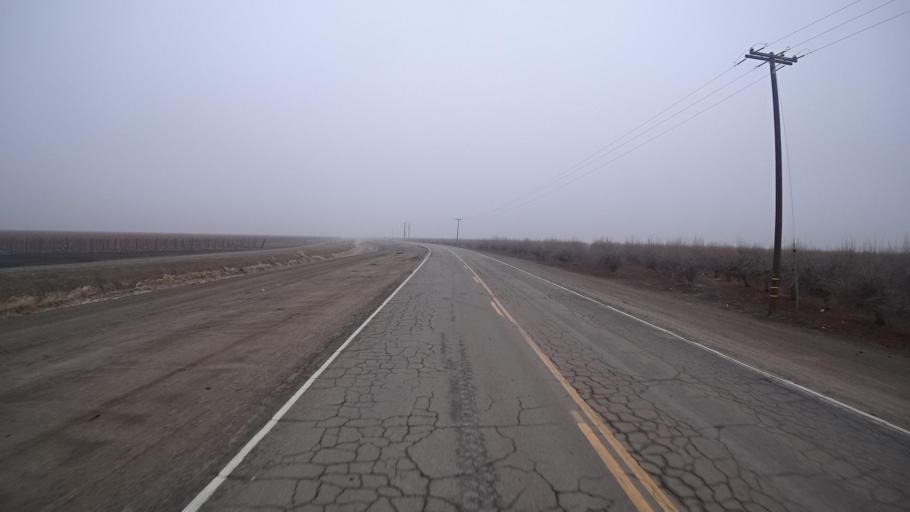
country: US
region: California
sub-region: Kern County
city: Lost Hills
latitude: 35.5131
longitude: -119.6148
